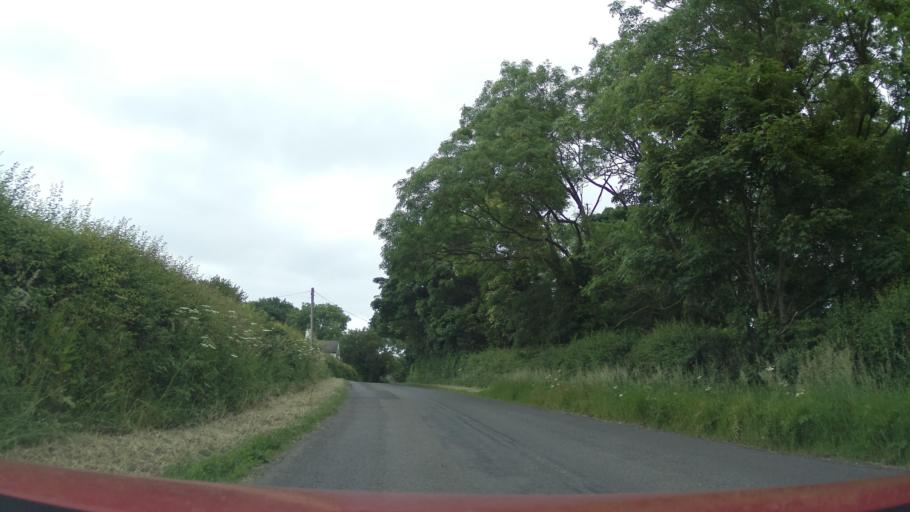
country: GB
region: England
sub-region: Leicestershire
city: Melton Mowbray
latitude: 52.7131
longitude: -0.8314
